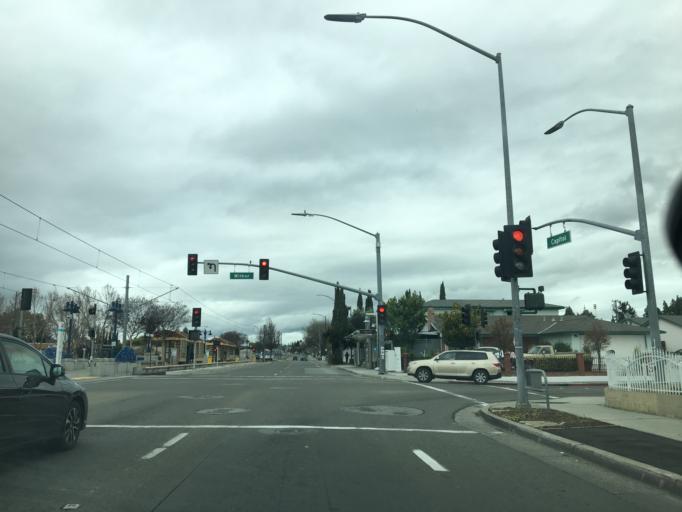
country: US
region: California
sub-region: Santa Clara County
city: Alum Rock
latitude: 37.3577
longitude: -121.8316
